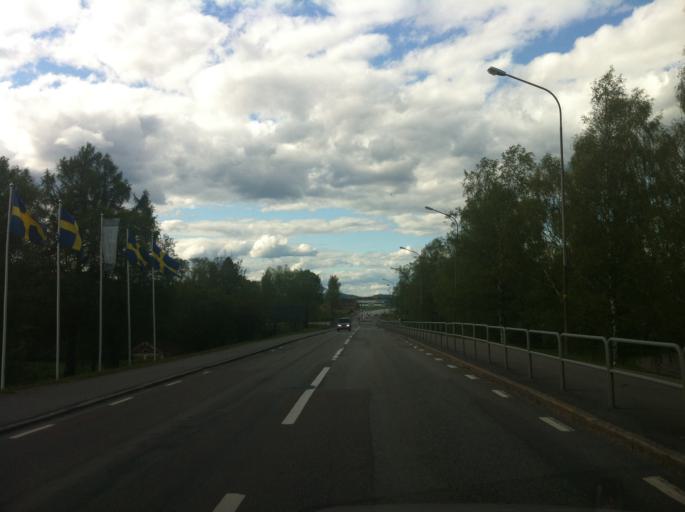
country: SE
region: Vaermland
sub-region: Storfors Kommun
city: Storfors
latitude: 59.5380
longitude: 14.2806
